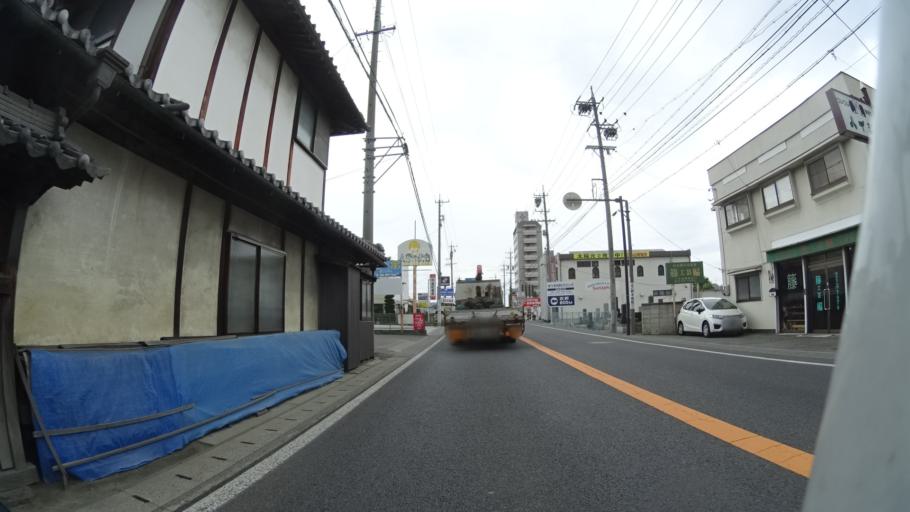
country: JP
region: Nagano
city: Nagano-shi
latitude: 36.5807
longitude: 138.1479
